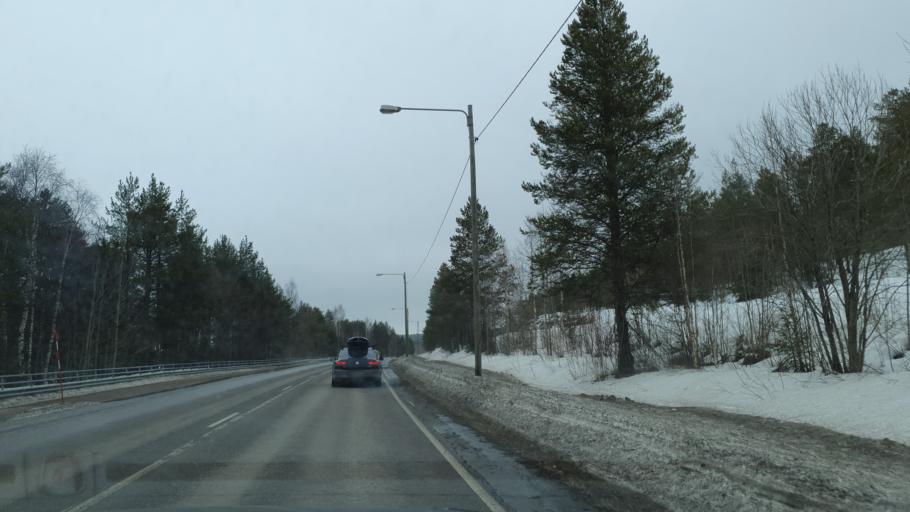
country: FI
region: Lapland
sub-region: Torniolaakso
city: Pello
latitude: 66.8110
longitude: 23.9978
